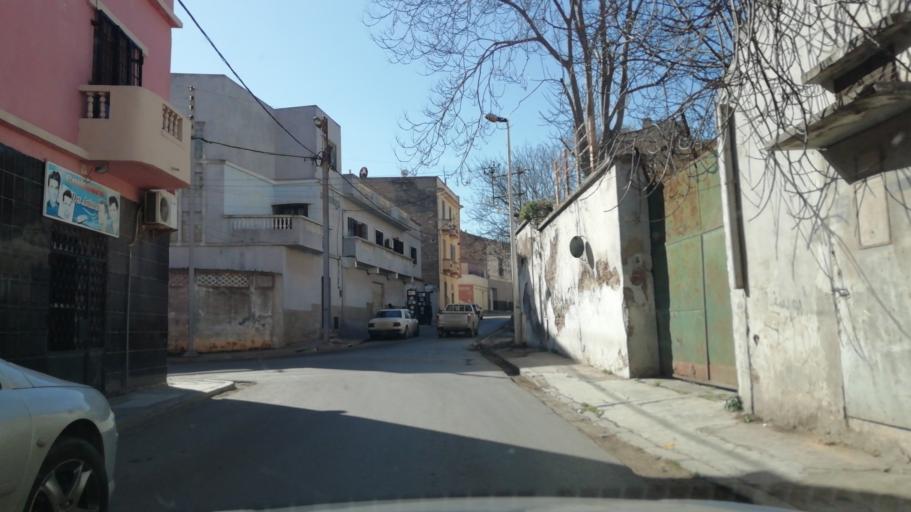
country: DZ
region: Oran
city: Oran
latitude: 35.7009
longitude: -0.6236
